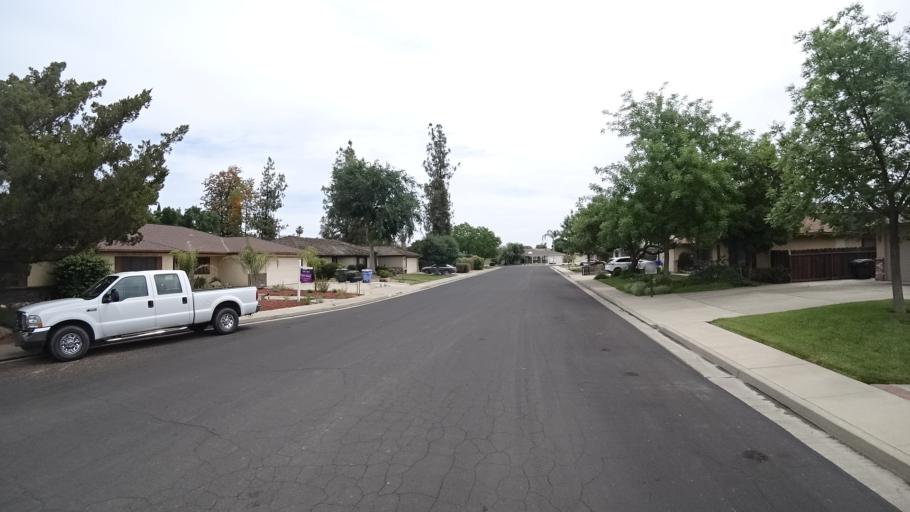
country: US
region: California
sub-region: Kings County
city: Lucerne
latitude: 36.3587
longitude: -119.6449
